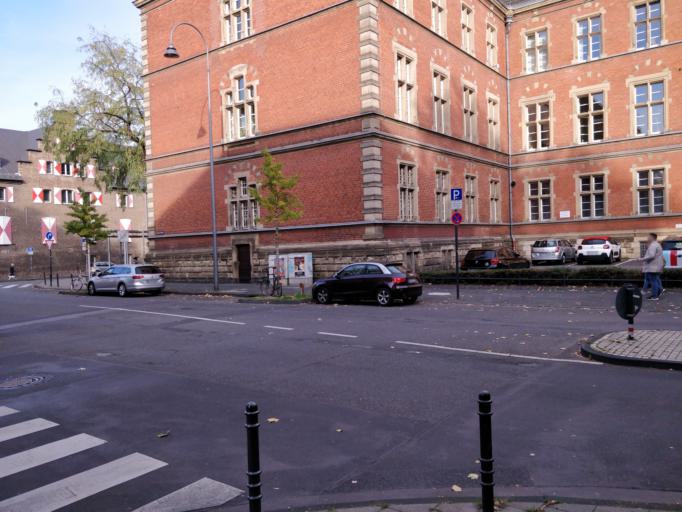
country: DE
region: North Rhine-Westphalia
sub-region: Regierungsbezirk Koln
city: Altstadt Nord
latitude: 50.9406
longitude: 6.9505
